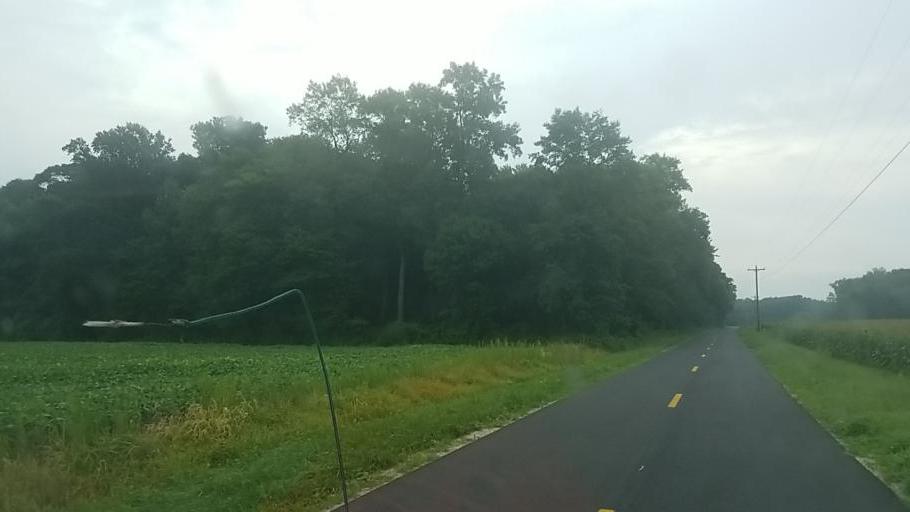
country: US
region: Delaware
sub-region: Sussex County
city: Selbyville
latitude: 38.4389
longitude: -75.2566
